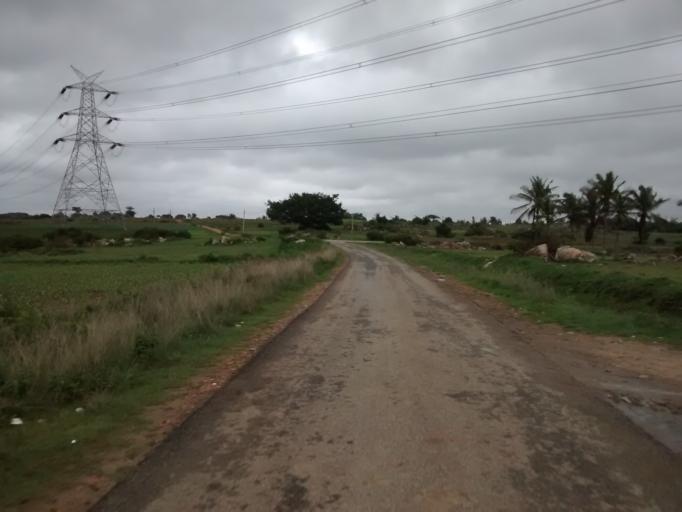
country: IN
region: Karnataka
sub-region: Hassan
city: Hassan
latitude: 12.9382
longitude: 76.1732
